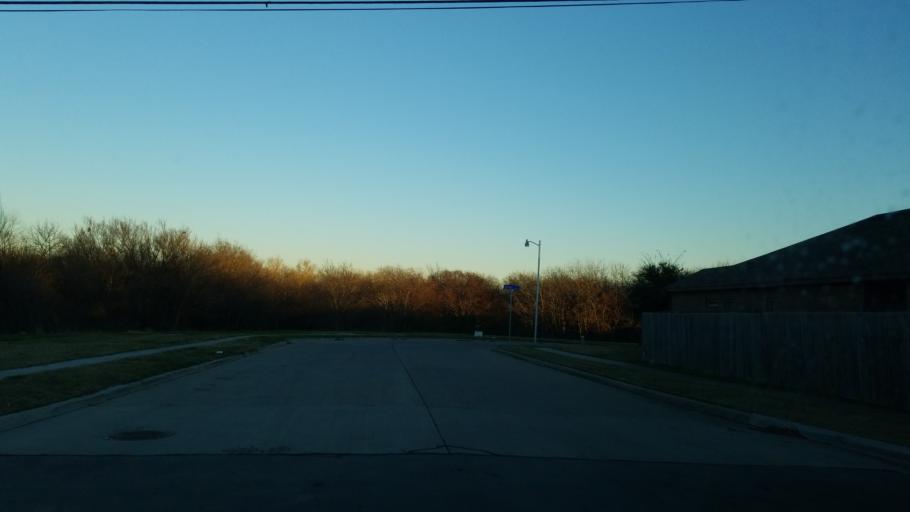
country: US
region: Texas
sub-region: Tarrant County
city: Arlington
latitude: 32.7261
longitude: -97.0568
